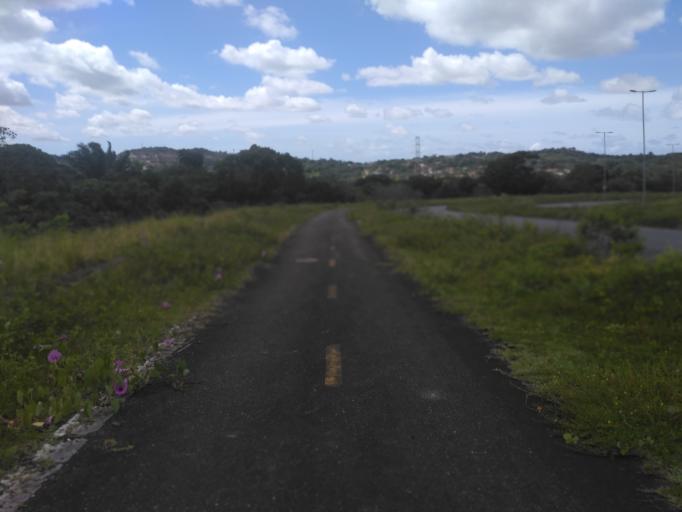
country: BR
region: Pernambuco
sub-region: Sao Lourenco Da Mata
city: Sao Lourenco da Mata
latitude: -8.0397
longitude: -35.0000
